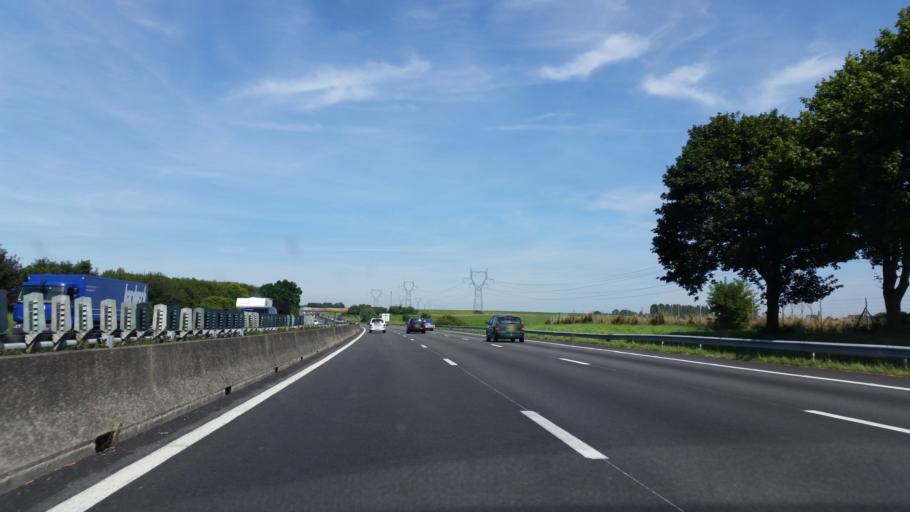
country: FR
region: Picardie
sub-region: Departement de la Somme
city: Peronne
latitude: 49.9042
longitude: 2.8492
